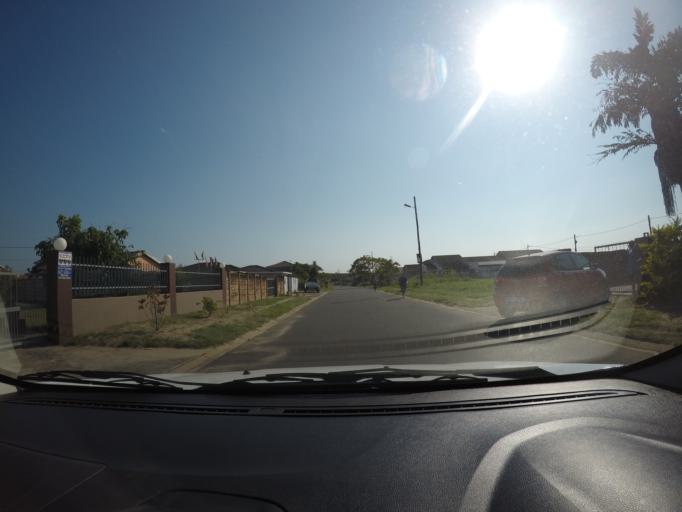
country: ZA
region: KwaZulu-Natal
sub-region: uThungulu District Municipality
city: Richards Bay
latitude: -28.7210
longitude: 32.0379
